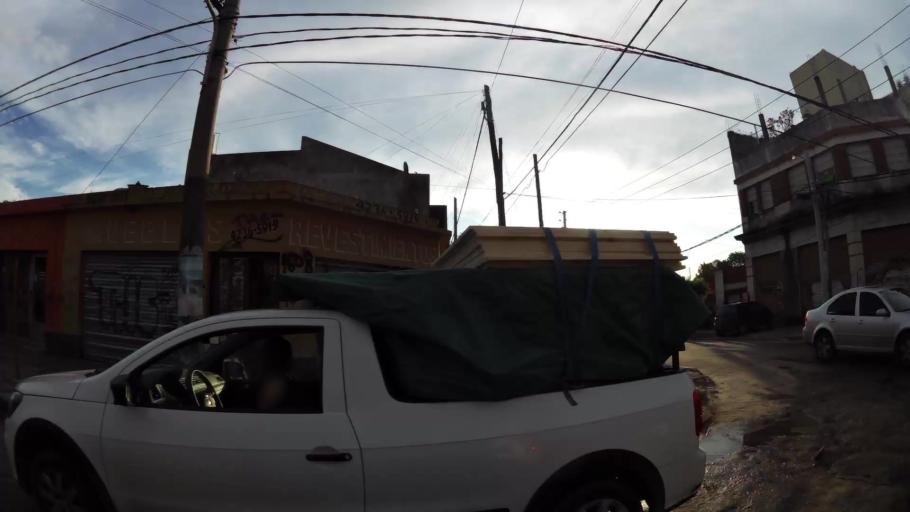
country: AR
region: Buenos Aires
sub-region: Partido de Almirante Brown
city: Adrogue
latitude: -34.7748
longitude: -58.3512
